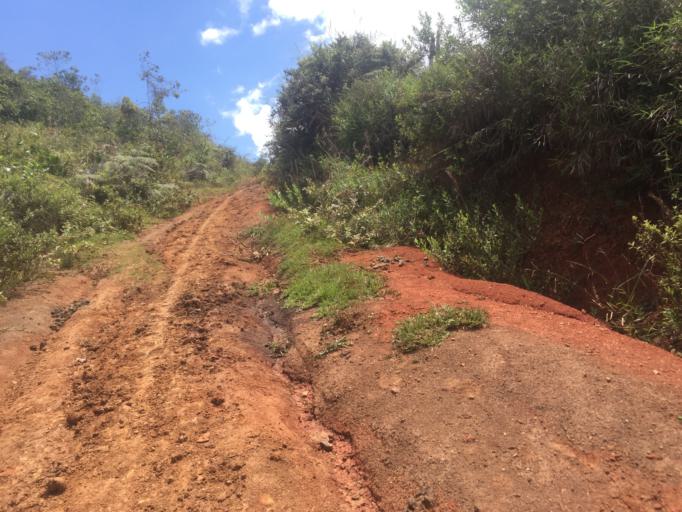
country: CO
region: Valle del Cauca
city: Dagua
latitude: 3.7135
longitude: -76.6023
